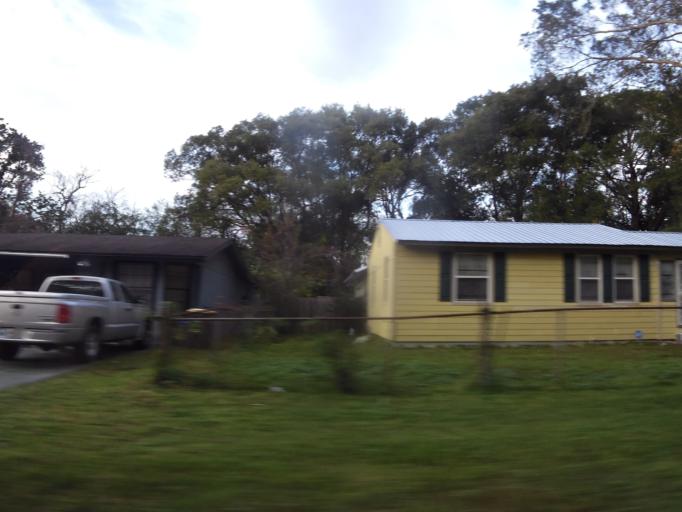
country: US
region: Florida
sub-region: Duval County
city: Jacksonville
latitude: 30.3534
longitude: -81.7177
